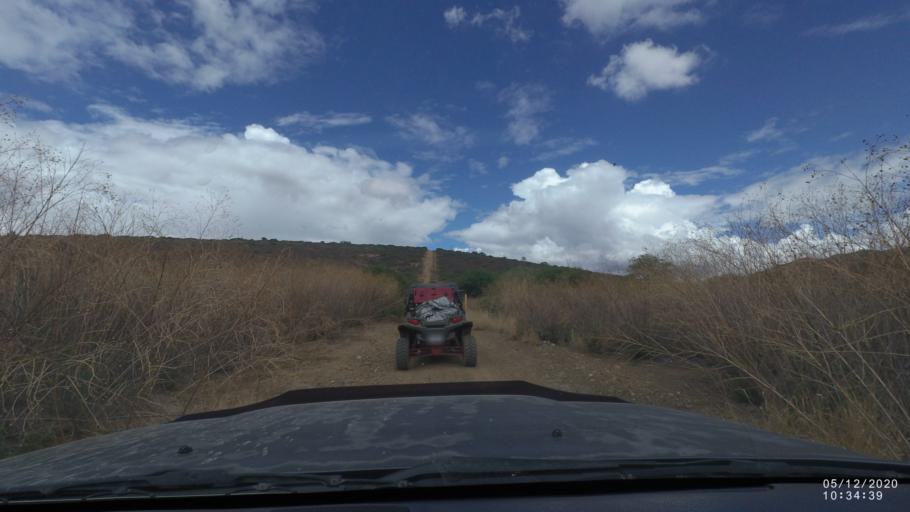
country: BO
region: Cochabamba
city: Sipe Sipe
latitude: -17.5457
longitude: -66.2788
